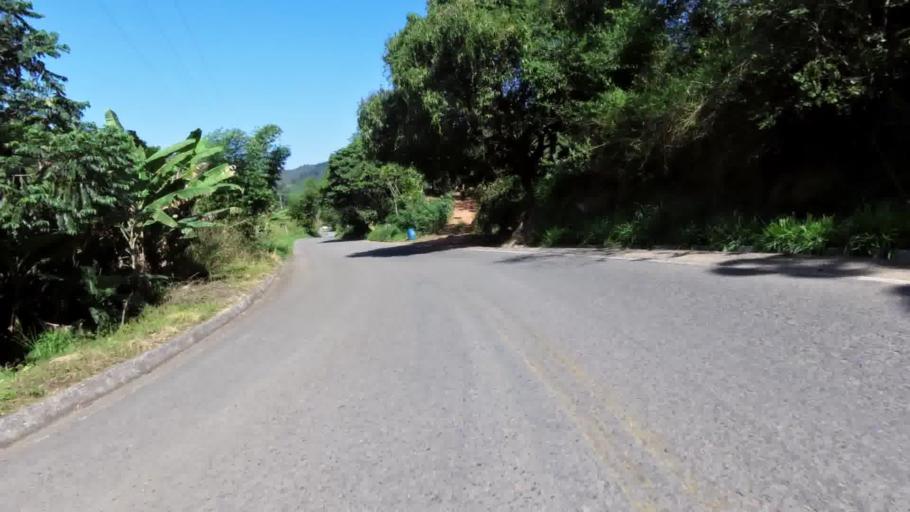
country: BR
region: Espirito Santo
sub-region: Alfredo Chaves
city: Alfredo Chaves
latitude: -20.5082
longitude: -40.7765
